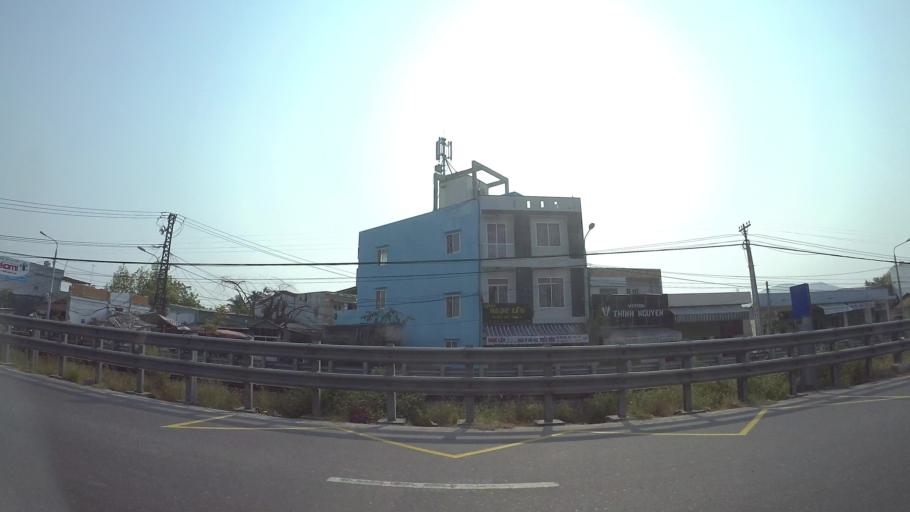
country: VN
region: Da Nang
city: Cam Le
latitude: 16.0217
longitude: 108.1935
